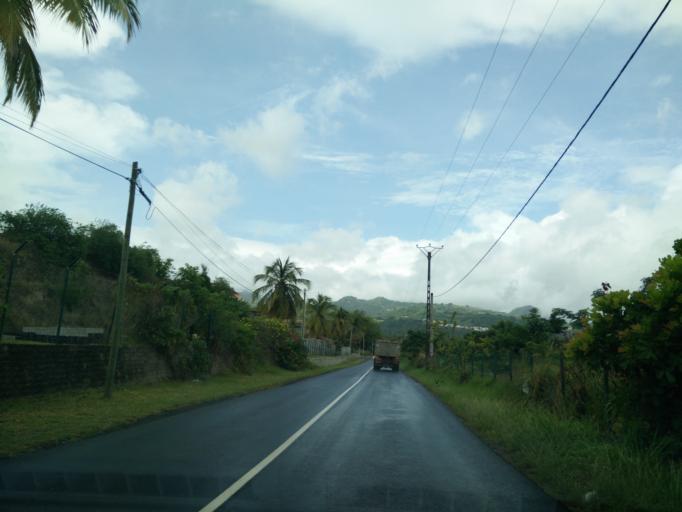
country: MQ
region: Martinique
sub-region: Martinique
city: Saint-Pierre
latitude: 14.7613
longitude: -61.1899
